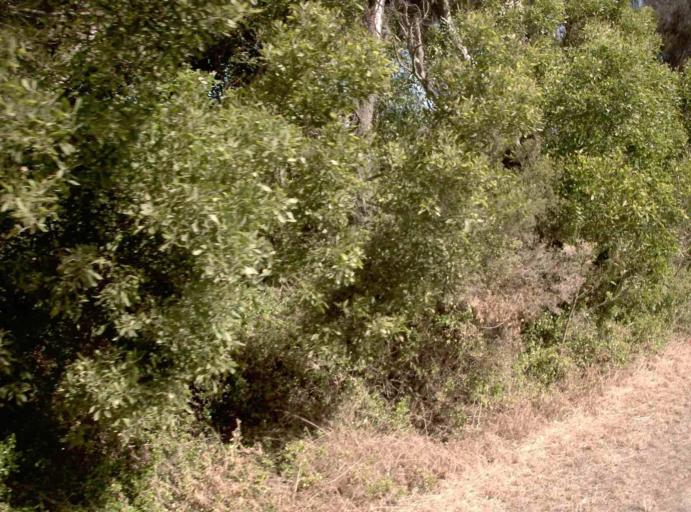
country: AU
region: Victoria
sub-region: Wellington
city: Sale
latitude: -38.3494
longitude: 147.1719
